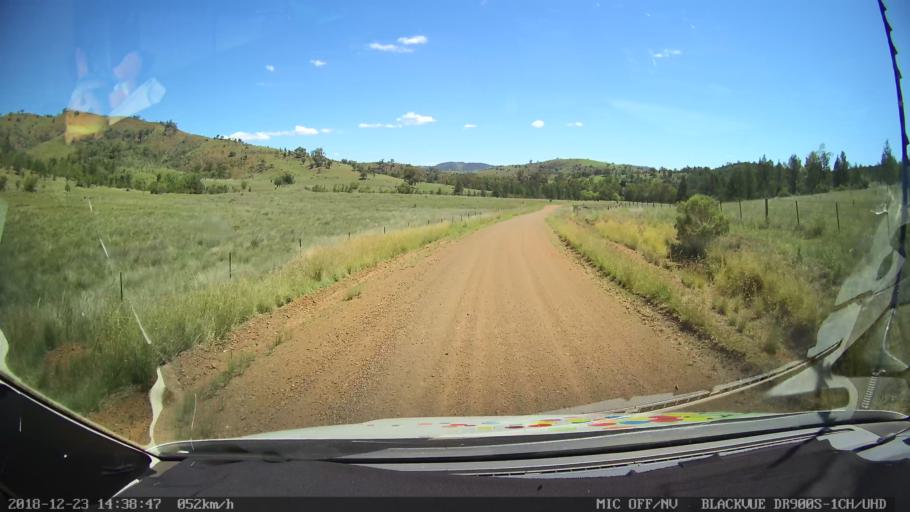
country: AU
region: New South Wales
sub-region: Tamworth Municipality
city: Manilla
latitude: -30.6236
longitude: 150.9050
